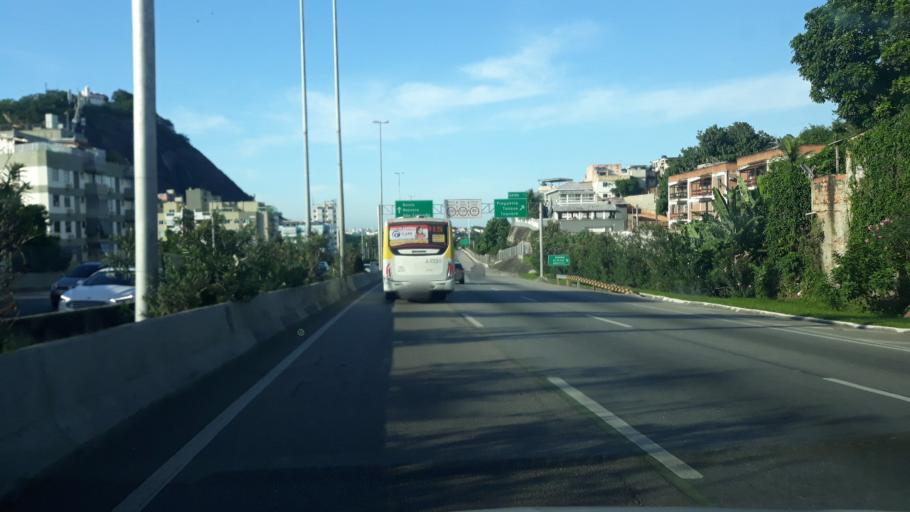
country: BR
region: Rio de Janeiro
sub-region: Sao Joao De Meriti
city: Sao Joao de Meriti
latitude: -22.9351
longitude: -43.3466
